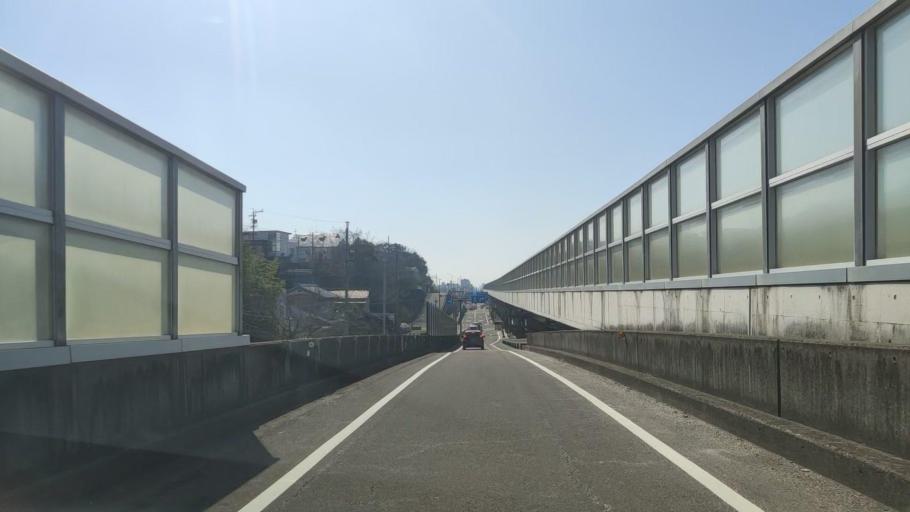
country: JP
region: Gifu
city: Gifu-shi
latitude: 35.4197
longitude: 136.7856
